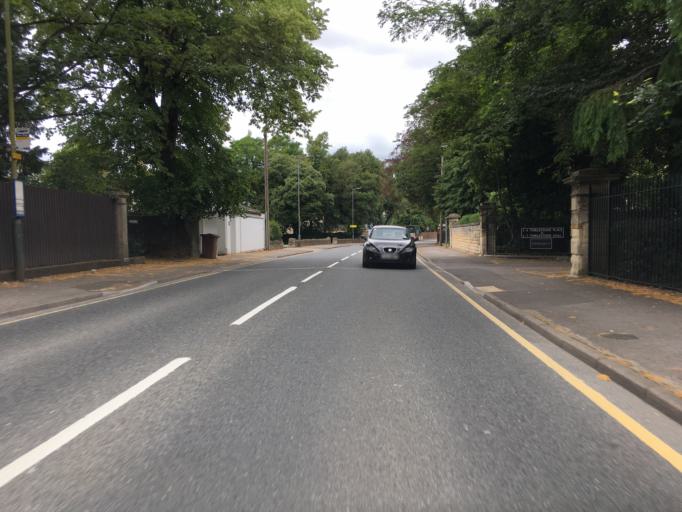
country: GB
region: England
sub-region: Gloucestershire
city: Cheltenham
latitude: 51.8885
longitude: -2.0692
